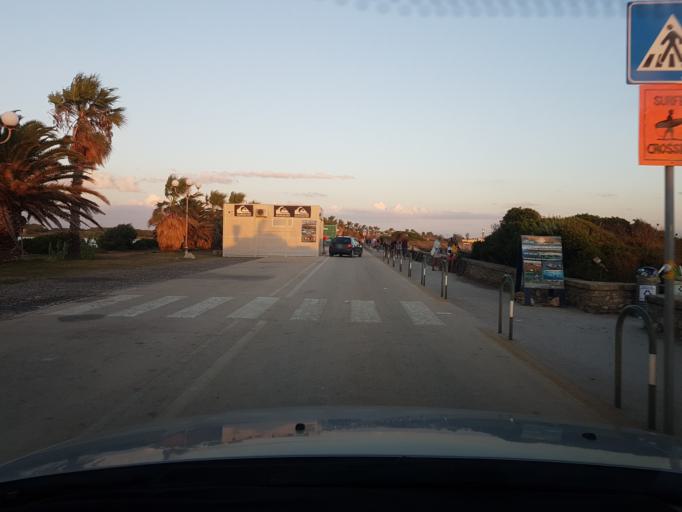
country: IT
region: Sardinia
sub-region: Provincia di Oristano
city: Riola Sardo
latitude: 40.0319
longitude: 8.4035
